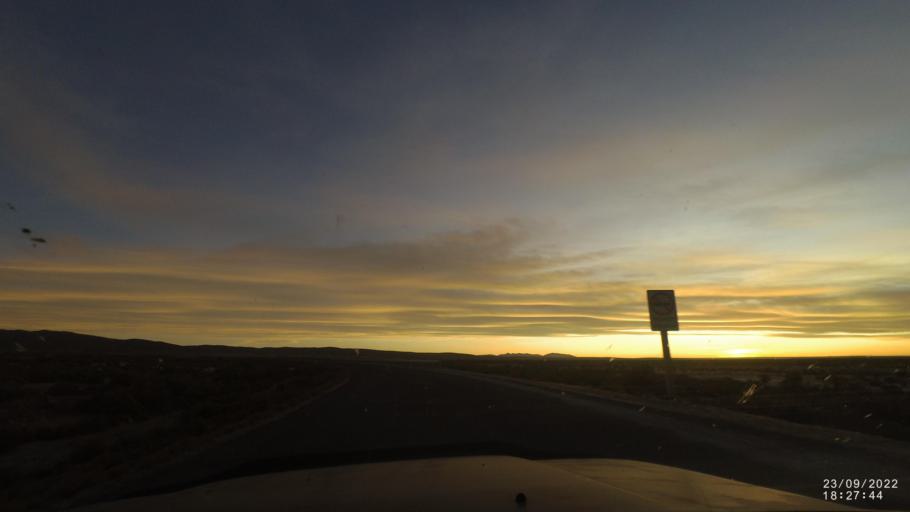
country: BO
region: Oruro
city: Challapata
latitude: -19.3304
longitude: -67.1715
